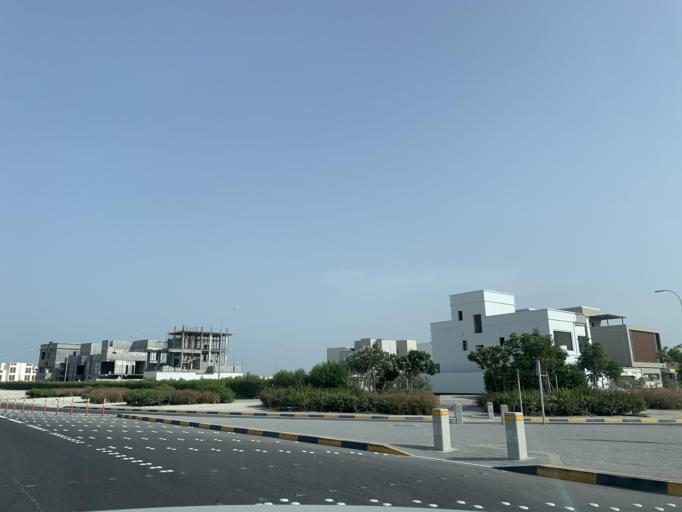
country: BH
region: Muharraq
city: Al Muharraq
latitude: 26.3134
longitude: 50.6337
